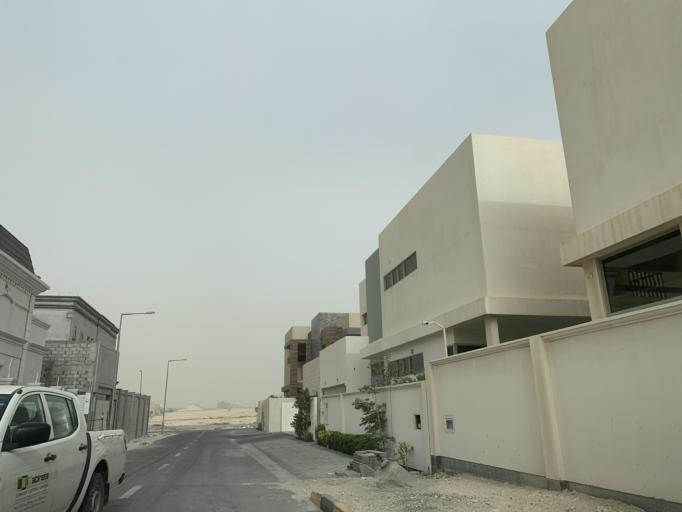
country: BH
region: Northern
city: Ar Rifa'
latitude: 26.1445
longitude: 50.5272
